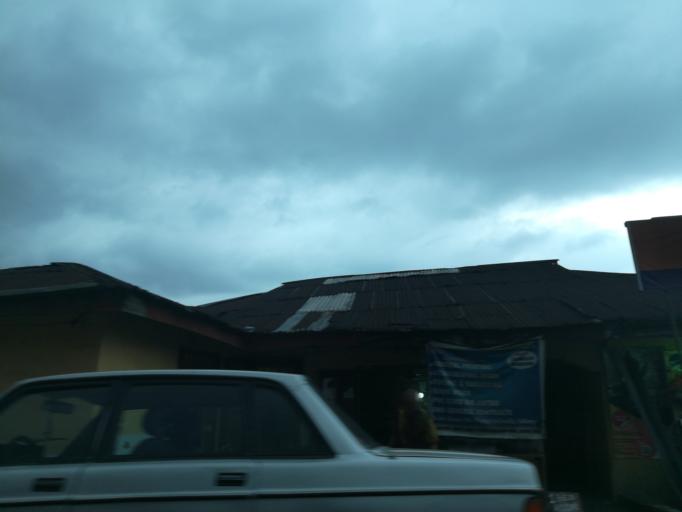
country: NG
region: Rivers
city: Port Harcourt
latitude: 4.7956
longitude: 6.9867
